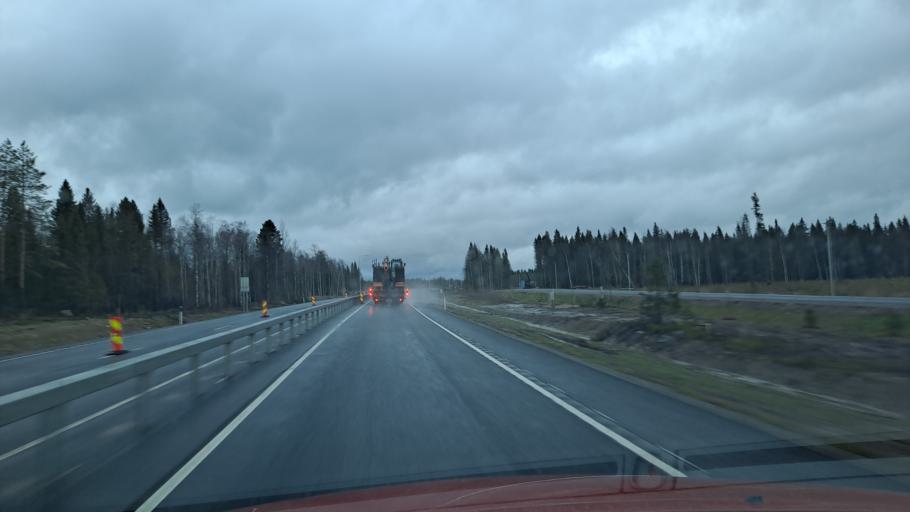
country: FI
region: Lapland
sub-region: Kemi-Tornio
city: Simo
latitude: 65.6769
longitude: 24.8083
